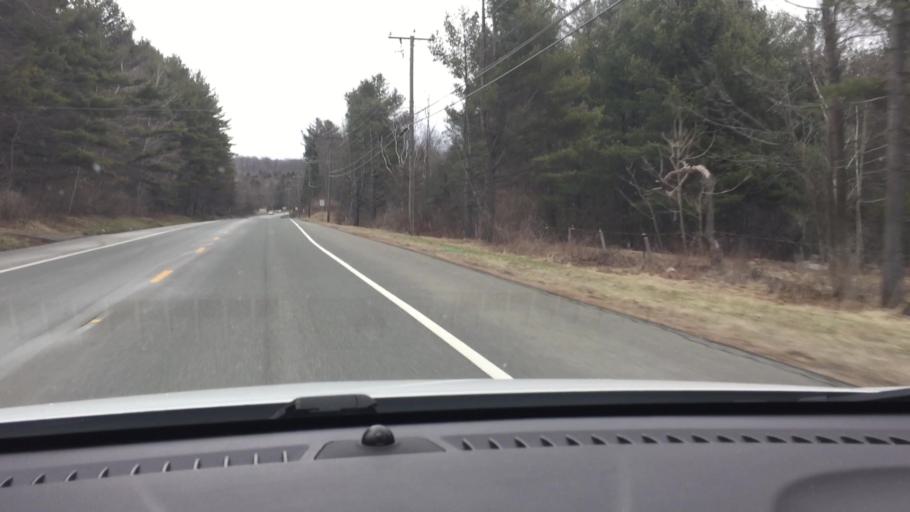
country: US
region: Massachusetts
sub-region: Berkshire County
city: Dalton
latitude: 42.4911
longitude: -73.1215
